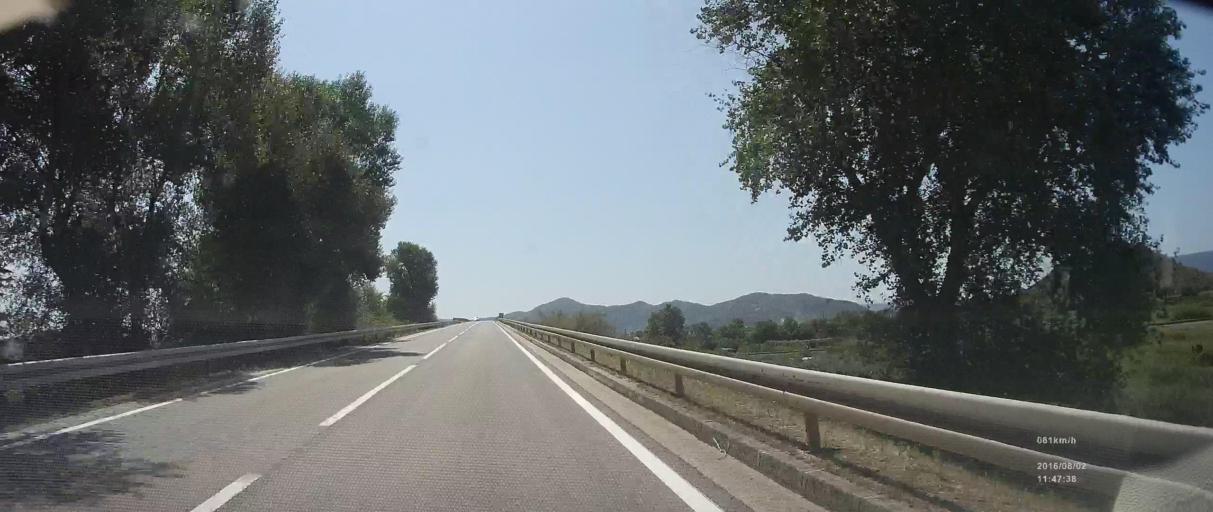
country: HR
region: Dubrovacko-Neretvanska
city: Komin
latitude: 43.0416
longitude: 17.4833
